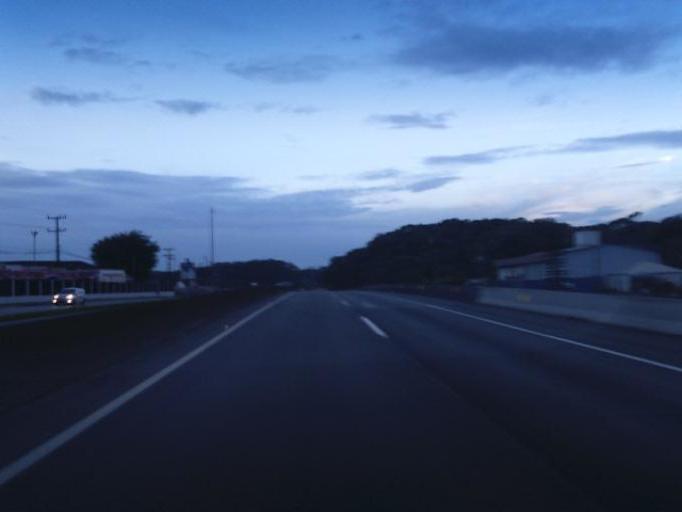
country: BR
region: Santa Catarina
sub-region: Joinville
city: Joinville
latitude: -26.2828
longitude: -48.8893
